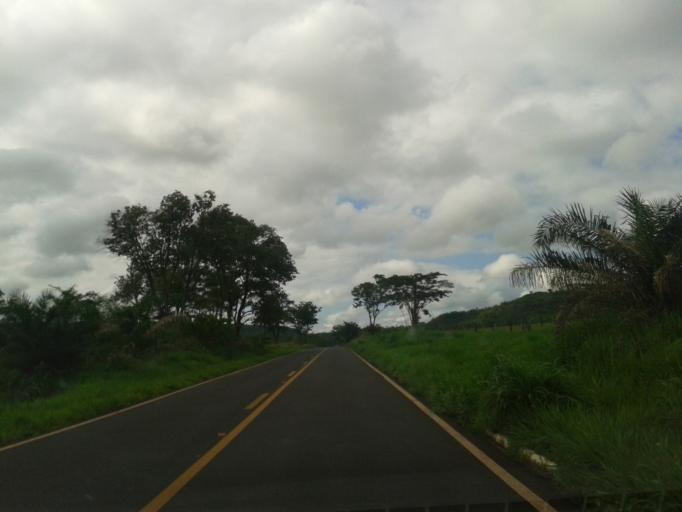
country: BR
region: Minas Gerais
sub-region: Ituiutaba
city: Ituiutaba
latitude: -19.1695
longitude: -49.7802
